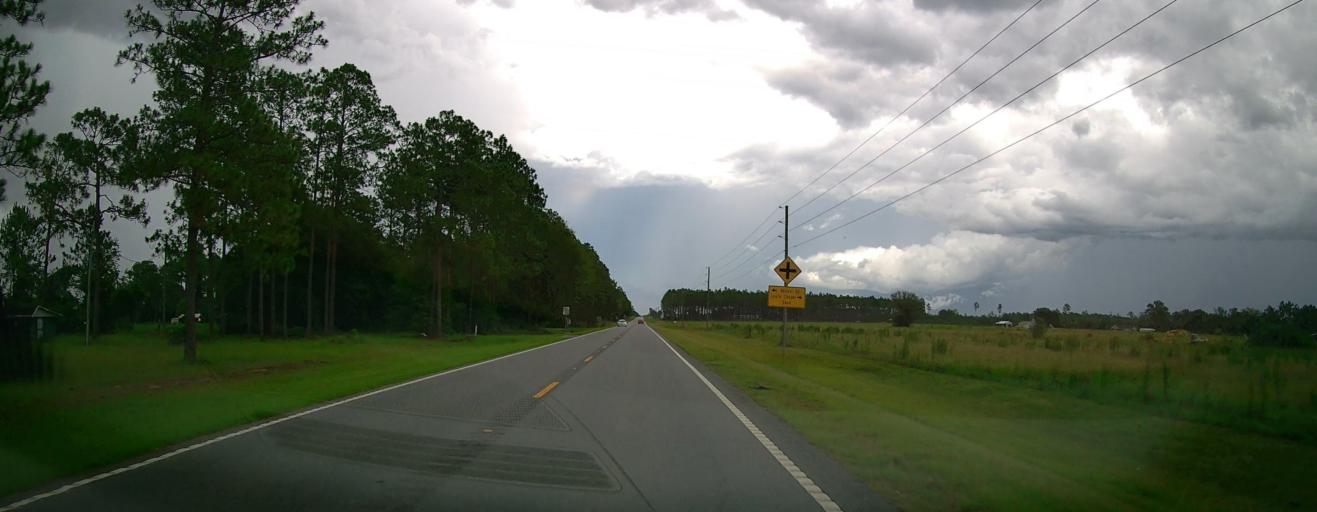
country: US
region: Georgia
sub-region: Pierce County
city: Blackshear
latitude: 31.3767
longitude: -82.1217
